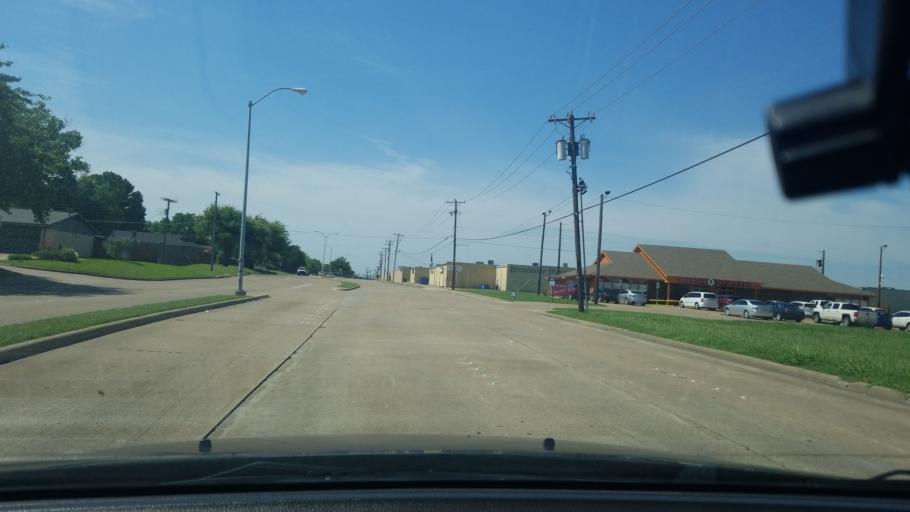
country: US
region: Texas
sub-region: Dallas County
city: Mesquite
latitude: 32.7740
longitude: -96.5971
